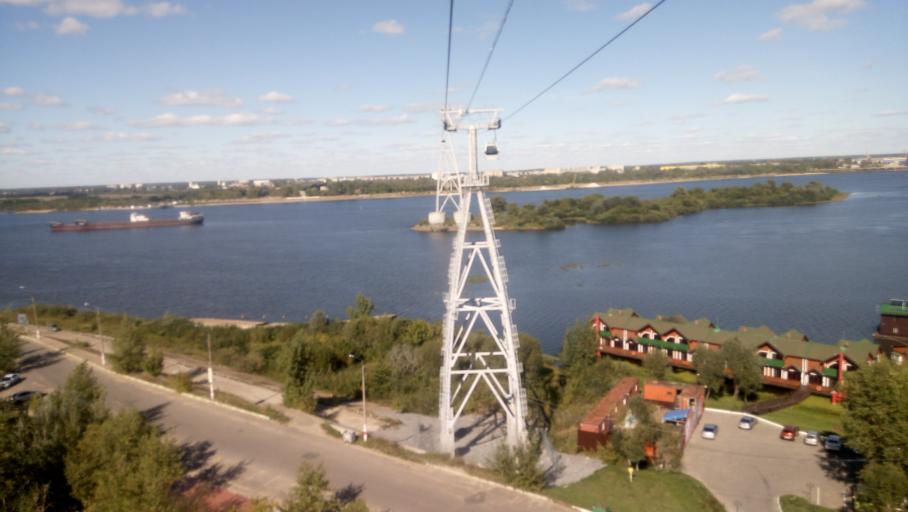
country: RU
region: Nizjnij Novgorod
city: Nizhniy Novgorod
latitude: 56.3292
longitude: 44.0431
